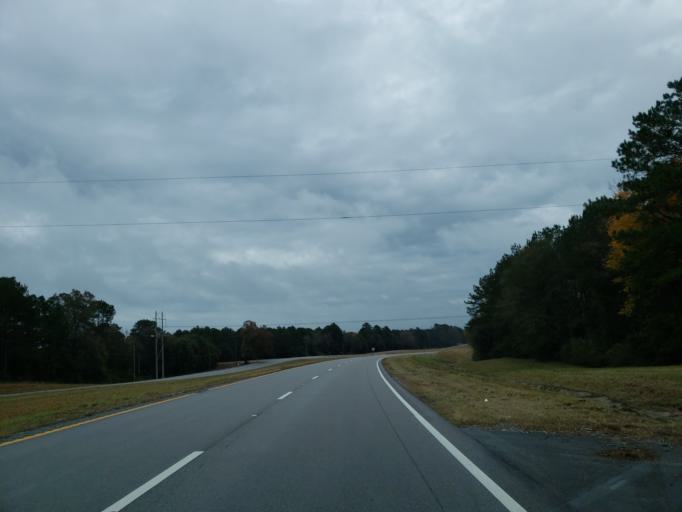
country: US
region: Mississippi
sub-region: Wayne County
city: Waynesboro
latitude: 31.6960
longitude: -88.7262
